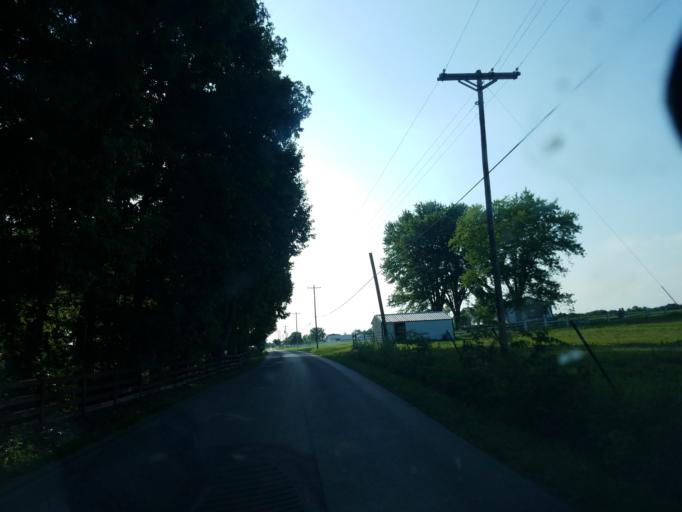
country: US
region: Ohio
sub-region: Adams County
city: West Union
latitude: 38.8767
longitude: -83.4844
